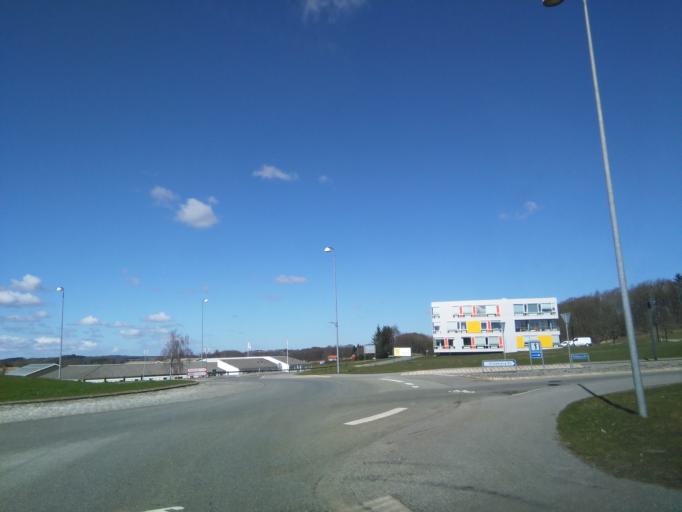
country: DK
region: Central Jutland
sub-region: Skanderborg Kommune
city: Ry
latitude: 56.0898
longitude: 9.7850
